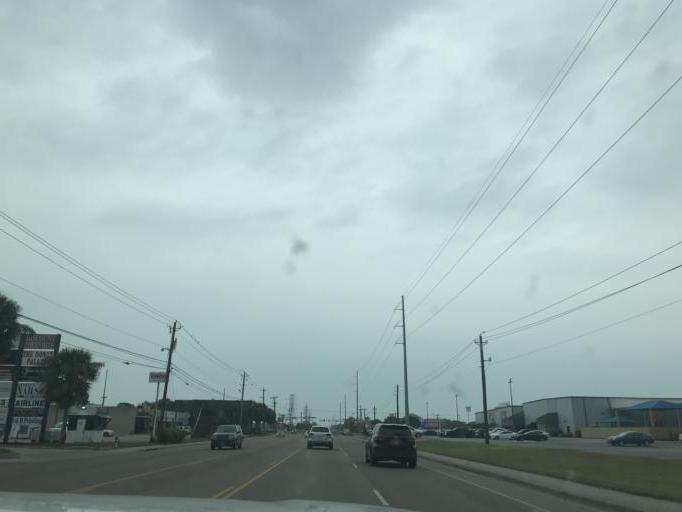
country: US
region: Texas
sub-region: Nueces County
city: Corpus Christi
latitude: 27.6932
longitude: -97.3657
